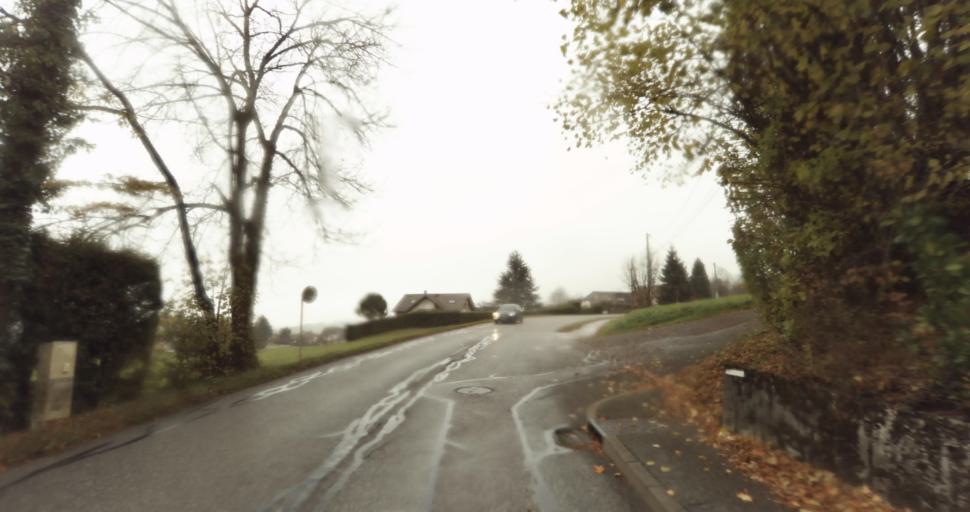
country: FR
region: Rhone-Alpes
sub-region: Departement de la Haute-Savoie
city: Villaz
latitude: 45.9469
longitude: 6.1743
